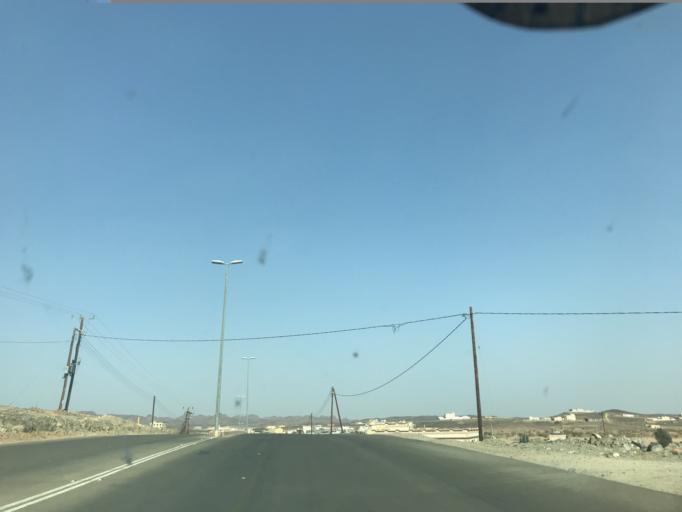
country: SA
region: Mintaqat al Bahah
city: Al Bahah
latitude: 20.4376
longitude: 41.9178
